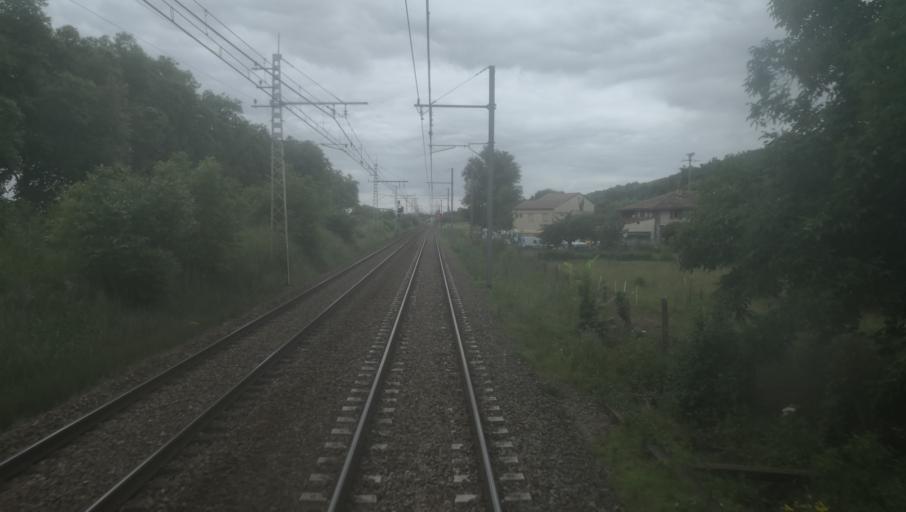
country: FR
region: Midi-Pyrenees
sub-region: Departement du Tarn-et-Garonne
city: Pompignan
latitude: 43.8038
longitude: 1.3244
